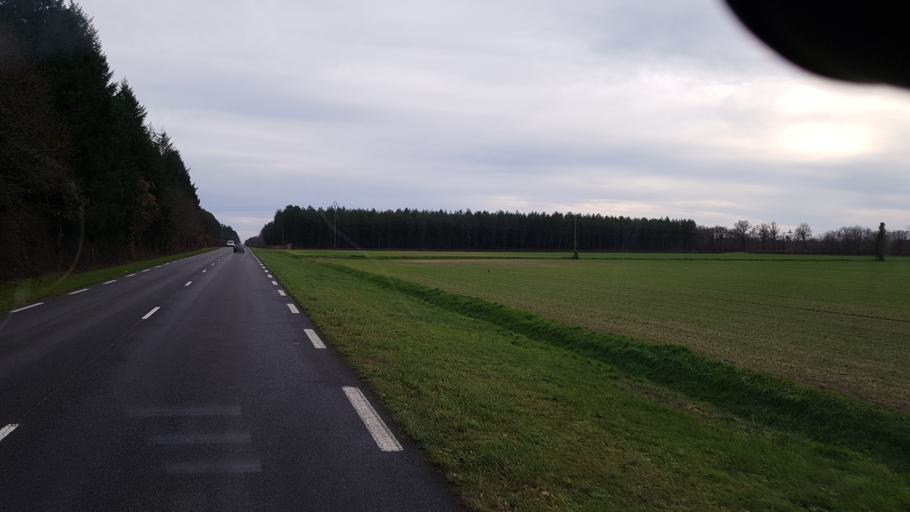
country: FR
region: Centre
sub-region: Departement du Loir-et-Cher
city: Lamotte-Beuvron
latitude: 47.6376
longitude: 1.9994
